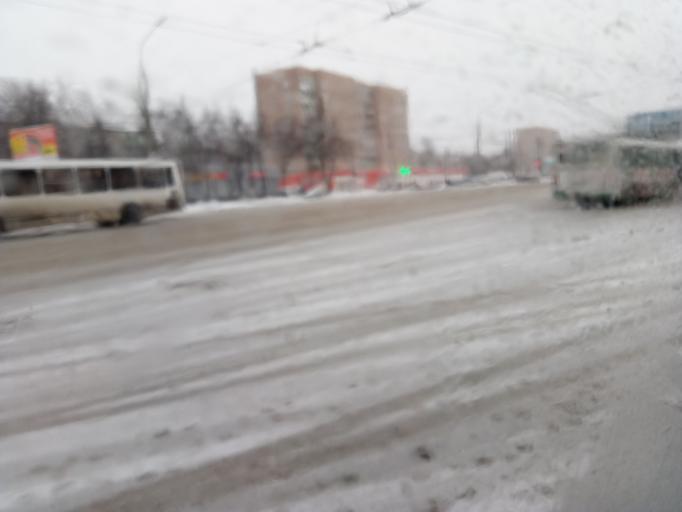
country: RU
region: Tula
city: Mendeleyevskiy
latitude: 54.1542
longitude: 37.5842
